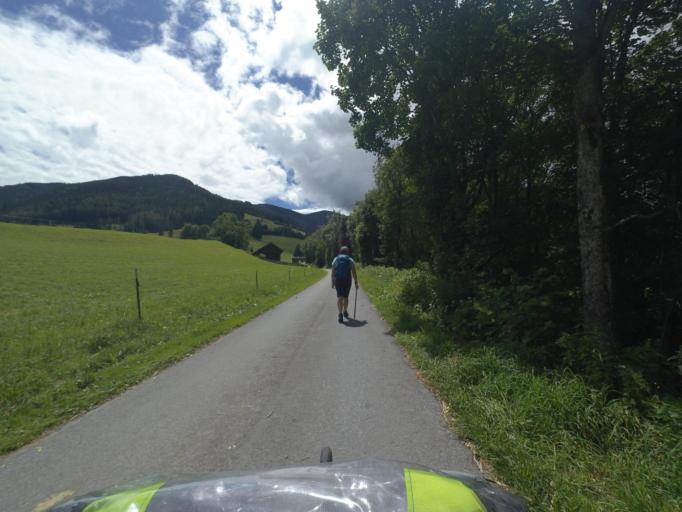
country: AT
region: Salzburg
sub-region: Politischer Bezirk Zell am See
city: Leogang
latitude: 47.4356
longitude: 12.7660
